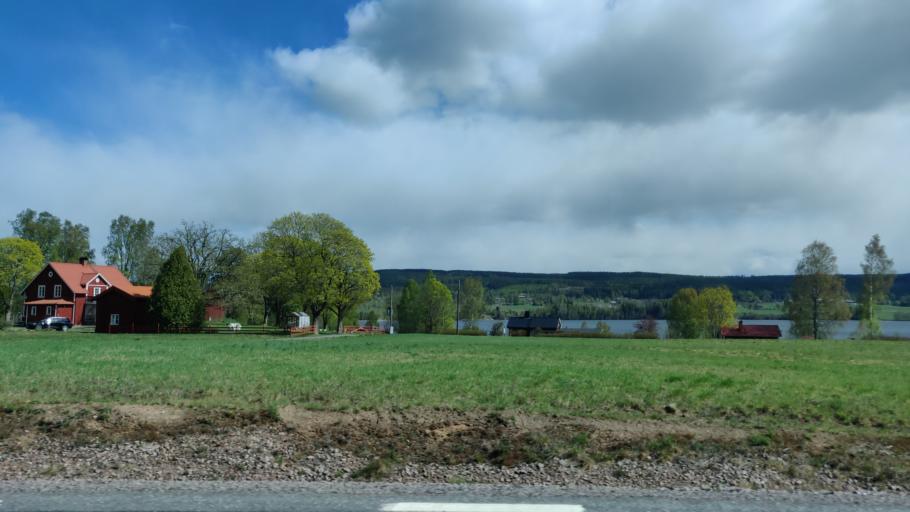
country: SE
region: Vaermland
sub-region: Munkfors Kommun
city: Munkfors
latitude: 59.8509
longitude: 13.7102
